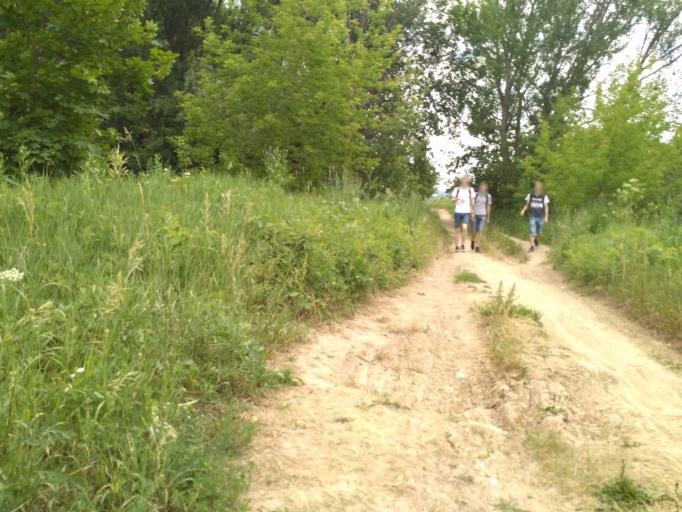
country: RU
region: Nizjnij Novgorod
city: Nizhniy Novgorod
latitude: 56.2767
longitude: 43.9712
